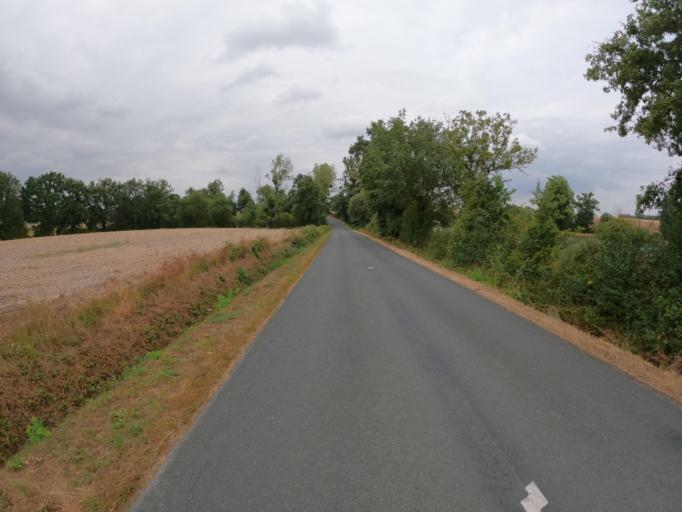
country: FR
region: Pays de la Loire
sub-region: Departement de la Vendee
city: Les Landes-Genusson
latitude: 46.9728
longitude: -1.1129
